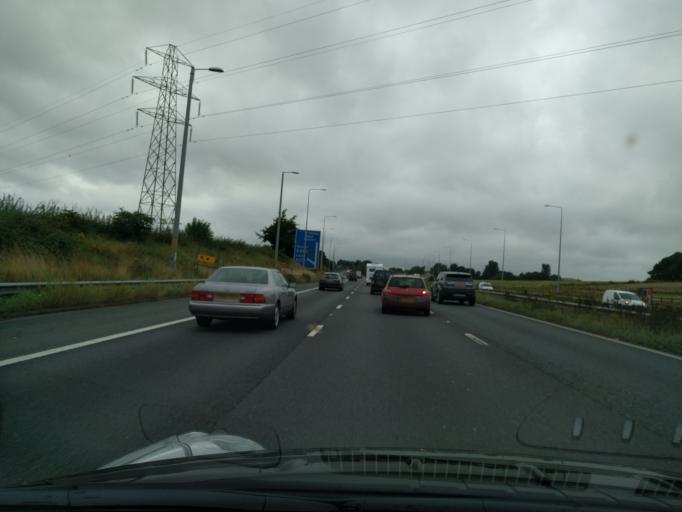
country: GB
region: England
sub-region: Warrington
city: Winwick
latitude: 53.4363
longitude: -2.5763
